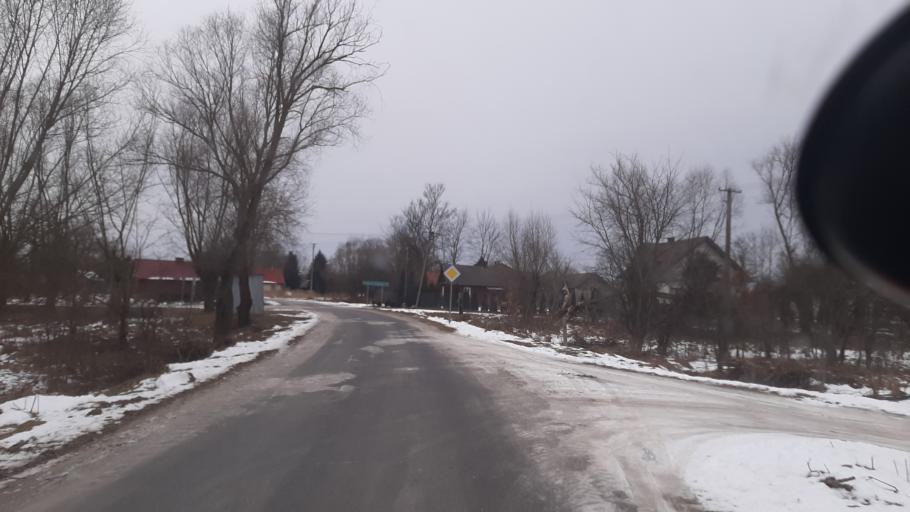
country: PL
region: Lublin Voivodeship
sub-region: Powiat lubartowski
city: Kamionka
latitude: 51.5182
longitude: 22.4759
